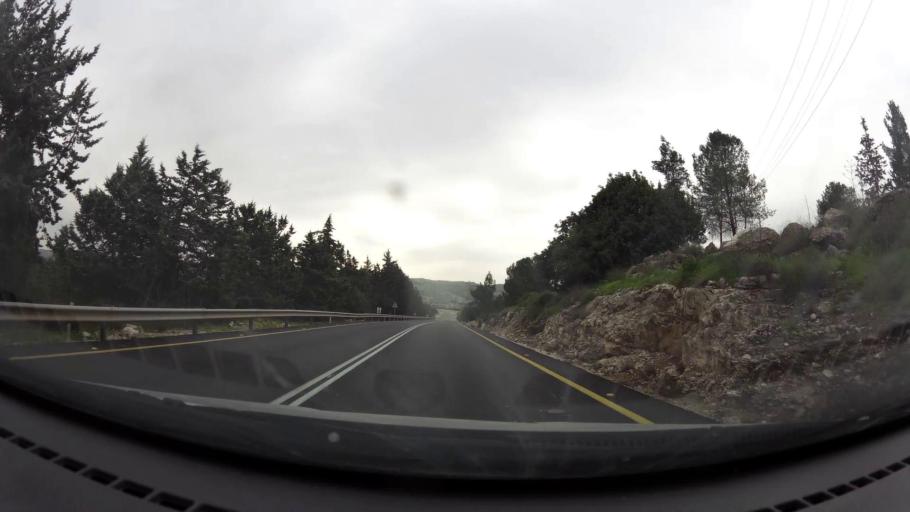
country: PS
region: West Bank
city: Surif
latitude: 31.6737
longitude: 35.0481
